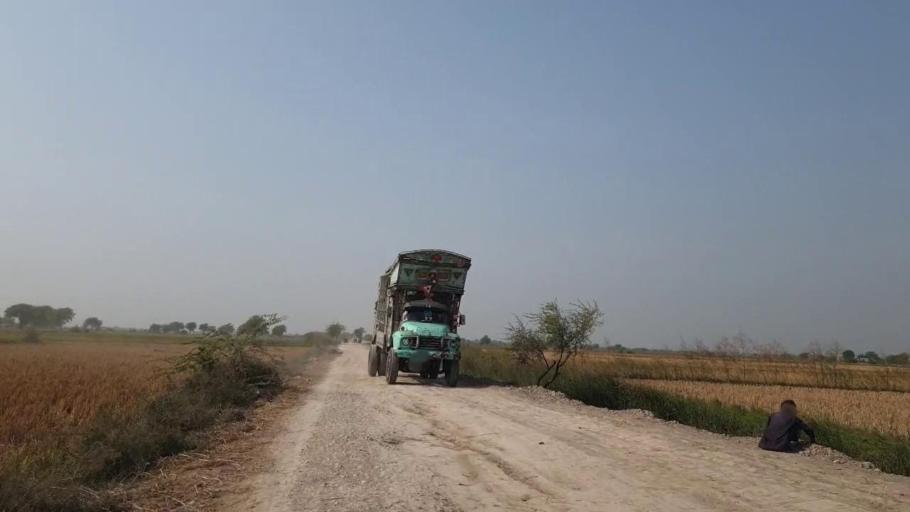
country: PK
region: Sindh
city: Kario
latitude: 24.9327
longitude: 68.5579
